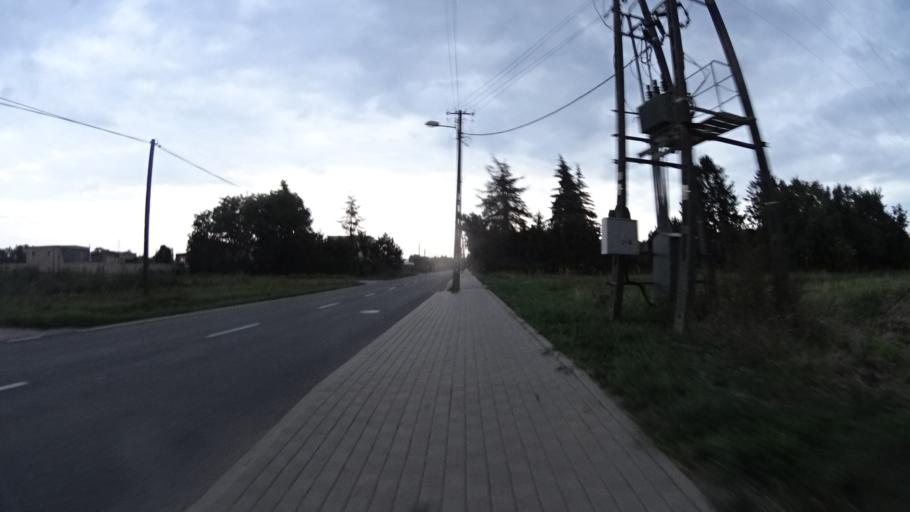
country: PL
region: Masovian Voivodeship
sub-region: Powiat warszawski zachodni
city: Babice
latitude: 52.2261
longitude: 20.8537
